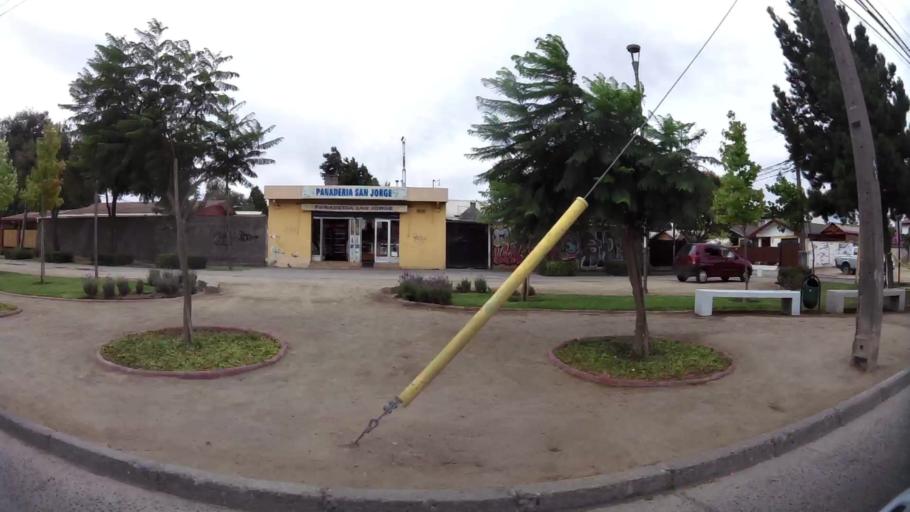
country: CL
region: O'Higgins
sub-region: Provincia de Cachapoal
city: Rancagua
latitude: -34.1479
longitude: -70.7390
